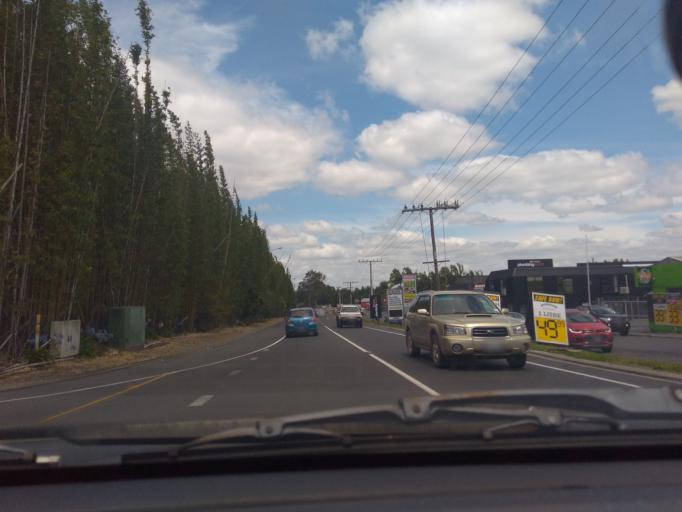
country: NZ
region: Northland
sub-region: Far North District
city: Kerikeri
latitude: -35.2066
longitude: 173.9177
